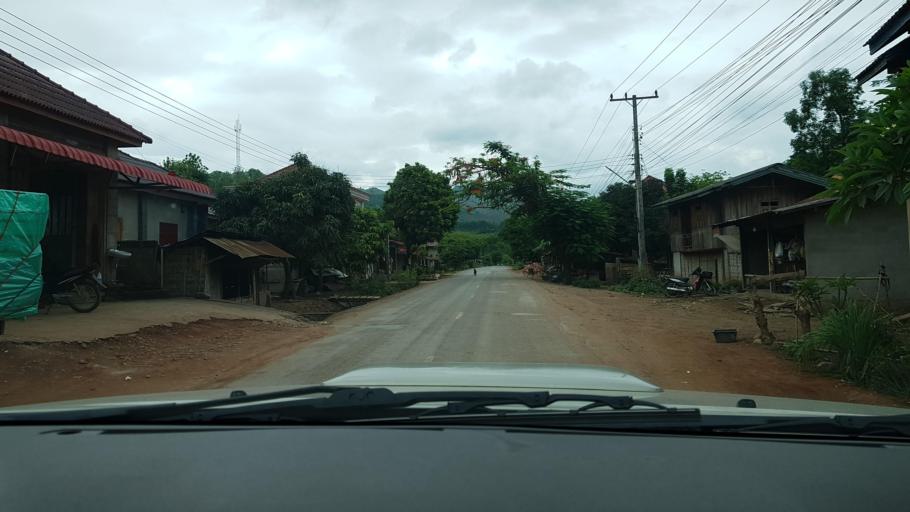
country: LA
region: Loungnamtha
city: Muang Nale
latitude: 20.2936
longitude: 101.6339
